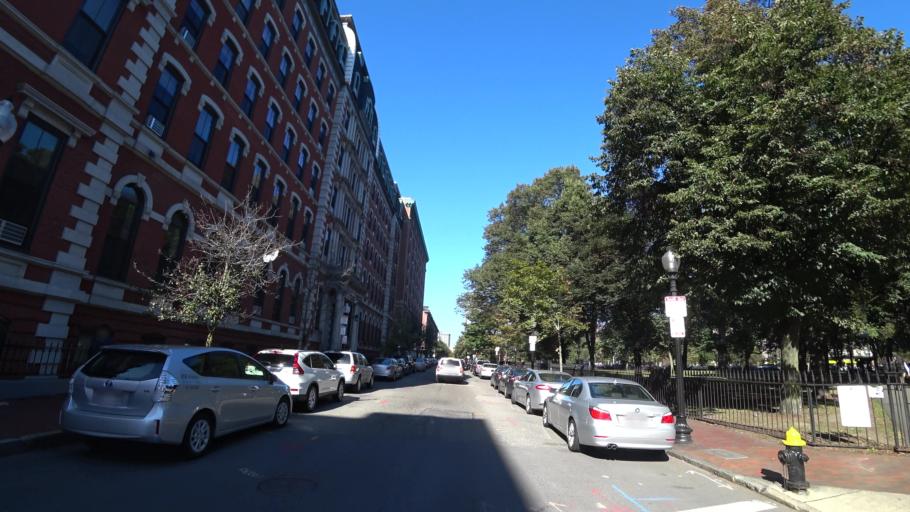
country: US
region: Massachusetts
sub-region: Suffolk County
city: South Boston
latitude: 42.3380
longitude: -71.0727
